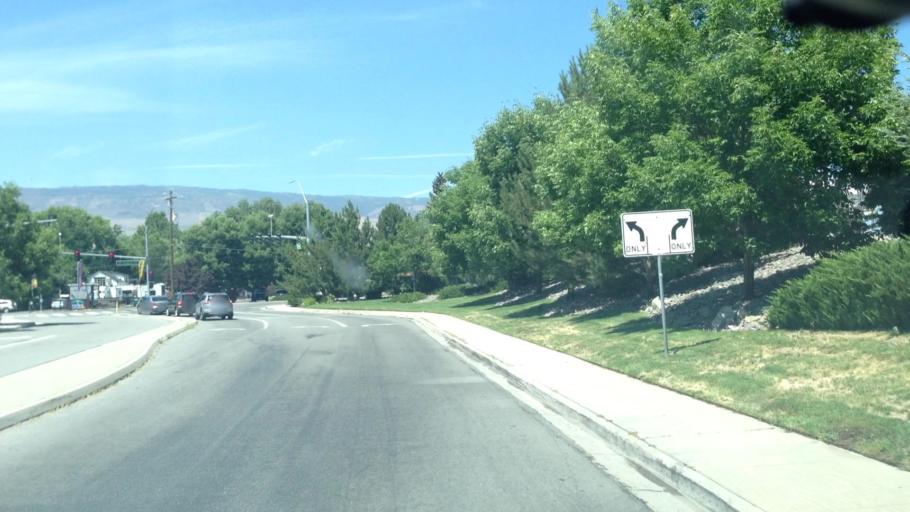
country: US
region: Nevada
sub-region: Washoe County
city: Sparks
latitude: 39.4422
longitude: -119.7704
